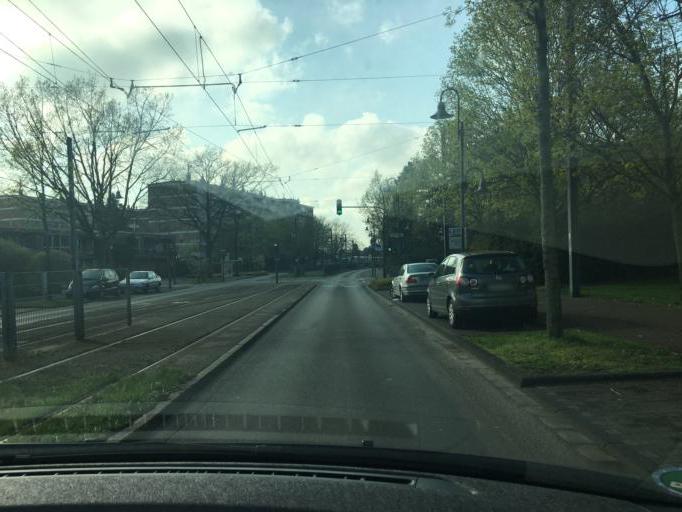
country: DE
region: North Rhine-Westphalia
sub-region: Regierungsbezirk Koln
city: Bonn
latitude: 50.7569
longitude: 7.0739
